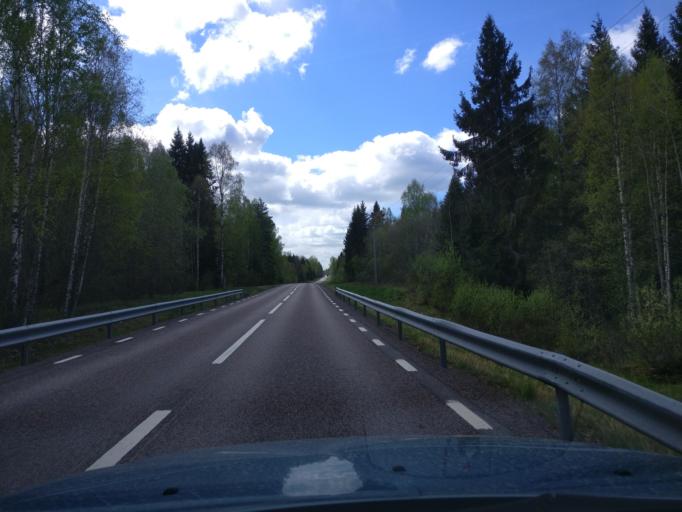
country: SE
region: Vaermland
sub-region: Karlstads Kommun
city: Molkom
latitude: 59.7576
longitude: 13.6930
